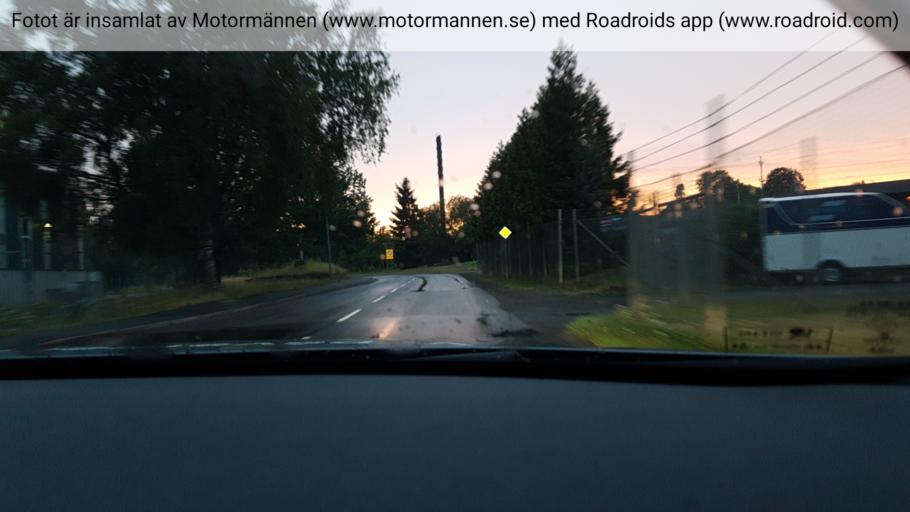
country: SE
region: Vaestra Goetaland
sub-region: Skovde Kommun
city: Skoevde
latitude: 58.4009
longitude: 13.8672
